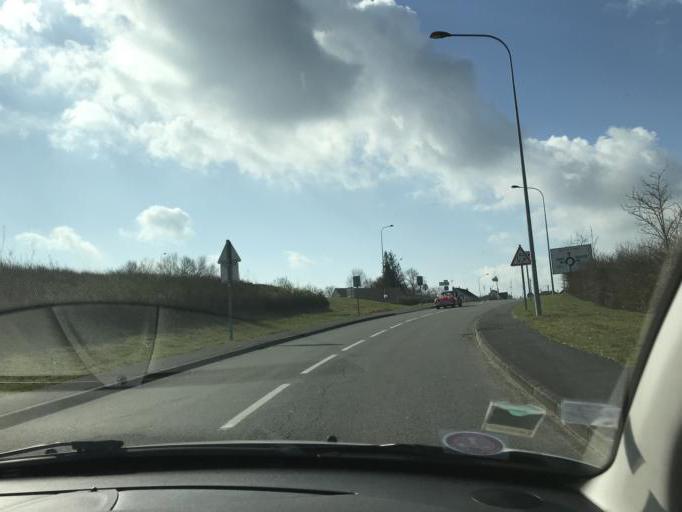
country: FR
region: Picardie
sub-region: Departement de l'Aisne
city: Venizel
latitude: 49.3635
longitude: 3.3910
